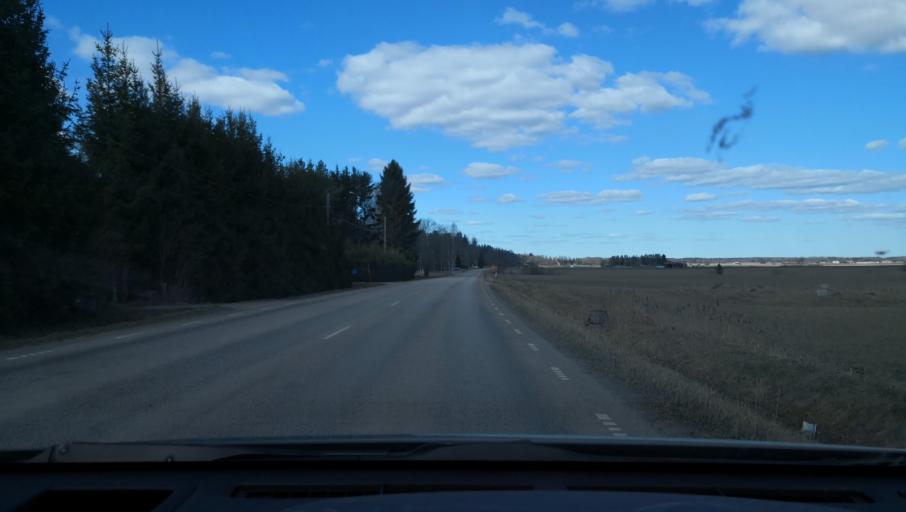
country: SE
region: Vaestmanland
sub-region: Sala Kommun
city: Sala
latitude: 59.9469
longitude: 16.6163
